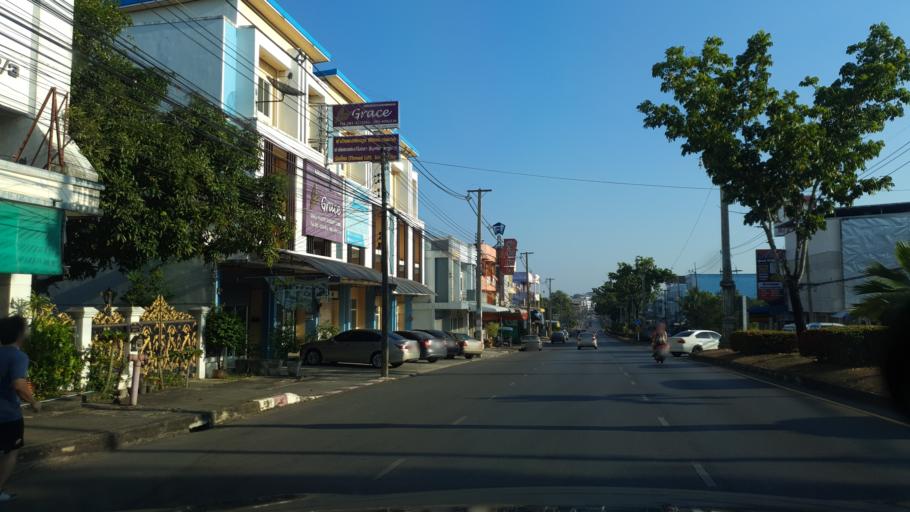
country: TH
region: Krabi
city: Krabi
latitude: 8.0742
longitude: 98.9107
